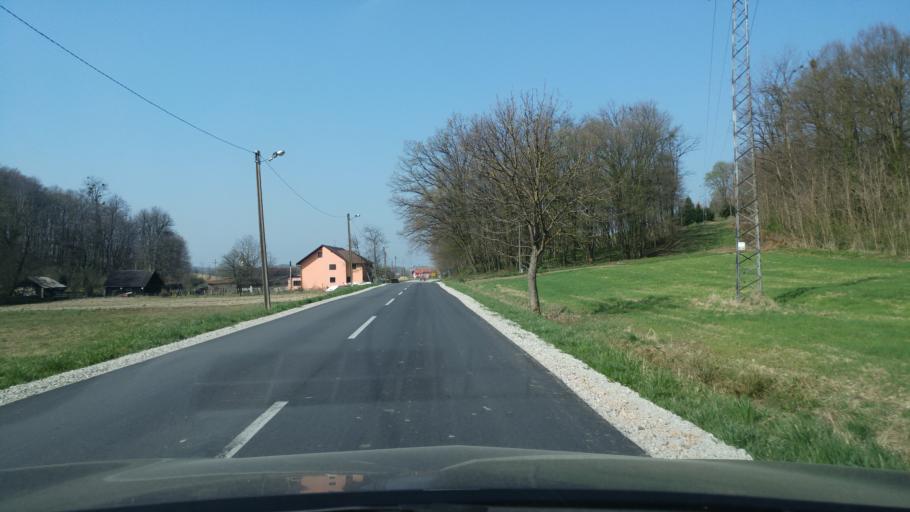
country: HR
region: Zagrebacka
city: Pojatno
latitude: 45.9530
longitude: 15.7388
